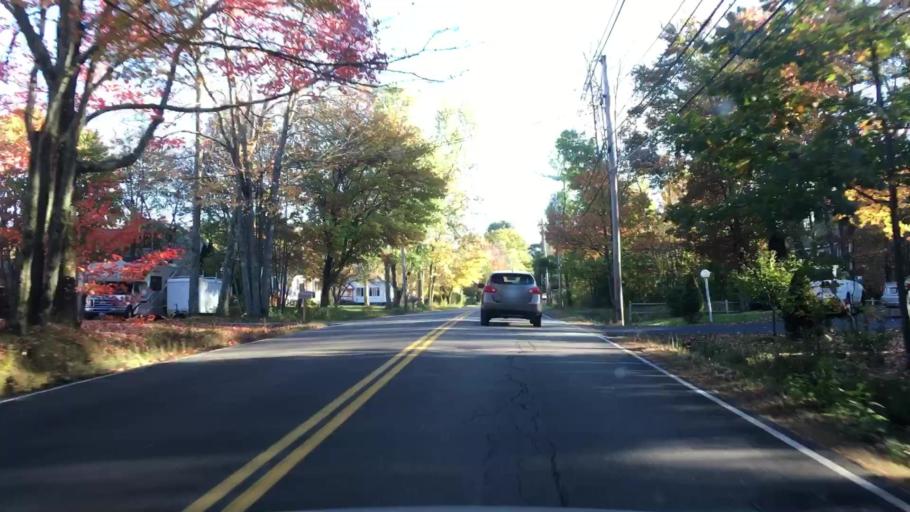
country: US
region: Maine
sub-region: Cumberland County
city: Scarborough
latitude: 43.6087
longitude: -70.3393
